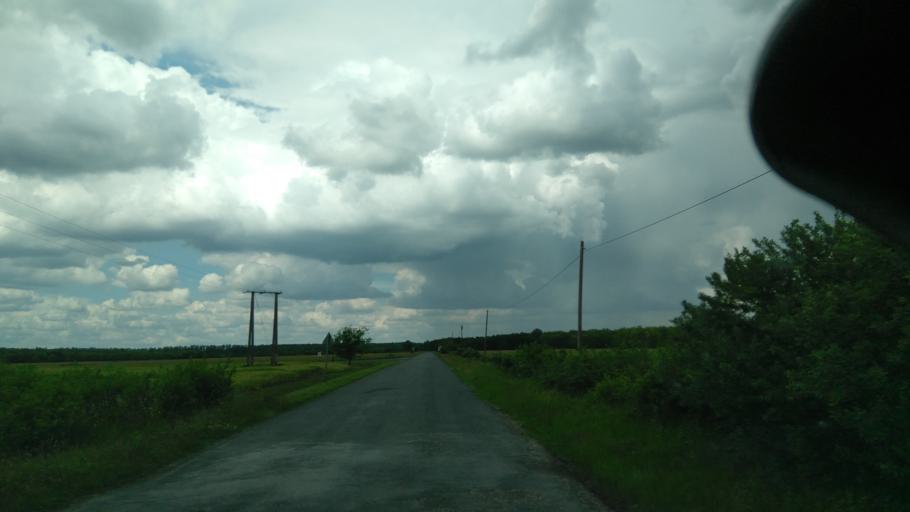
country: HU
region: Bekes
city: Szeghalom
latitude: 47.1030
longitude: 21.0801
